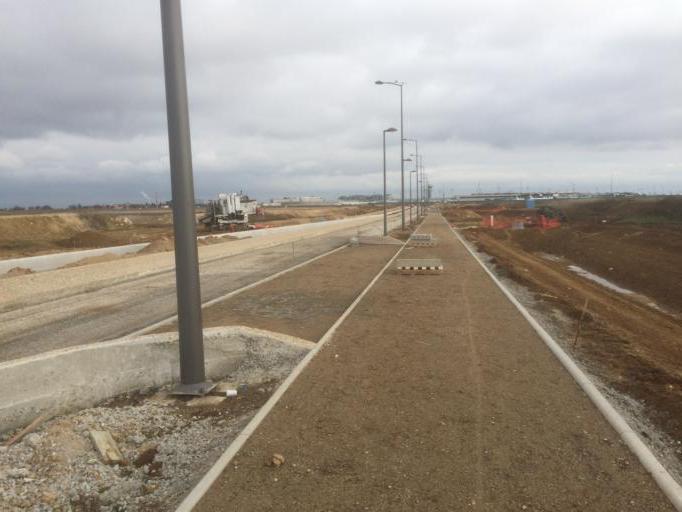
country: FR
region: Ile-de-France
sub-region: Departement du Val-de-Marne
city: Rungis
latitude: 48.7362
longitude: 2.3485
